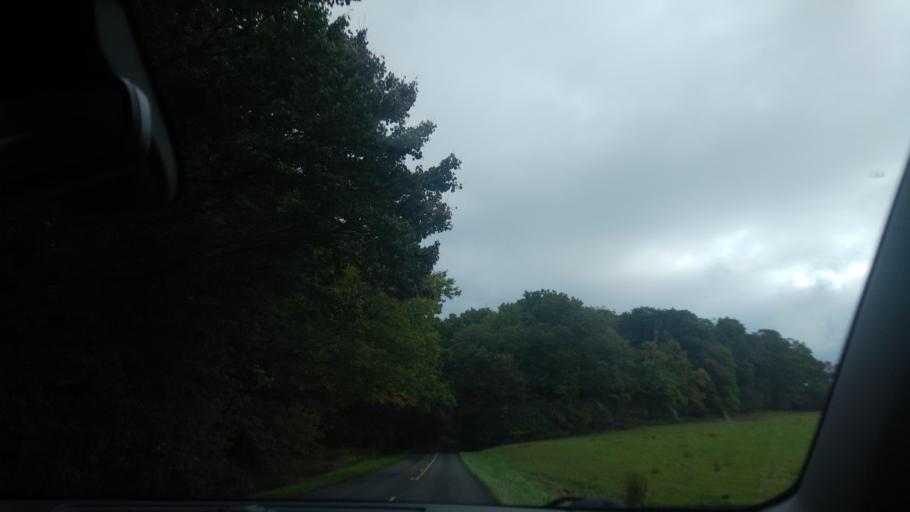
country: US
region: Virginia
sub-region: Carroll County
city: Cana
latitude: 36.6544
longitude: -80.5572
